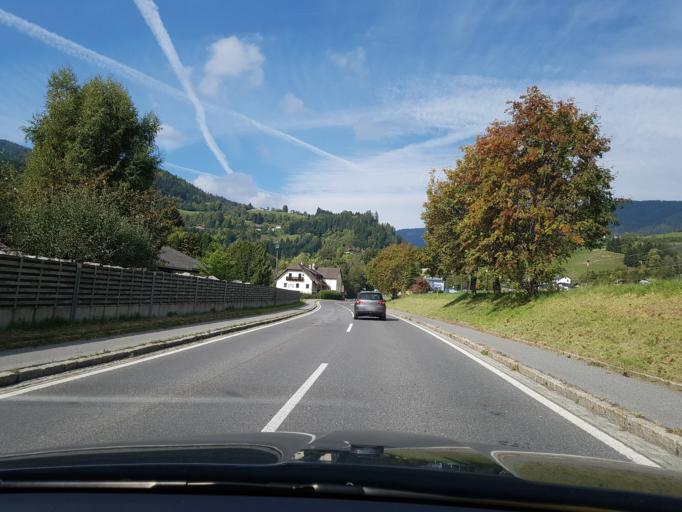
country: AT
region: Carinthia
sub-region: Politischer Bezirk Feldkirchen
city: Himmelberg
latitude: 46.7545
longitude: 14.0317
